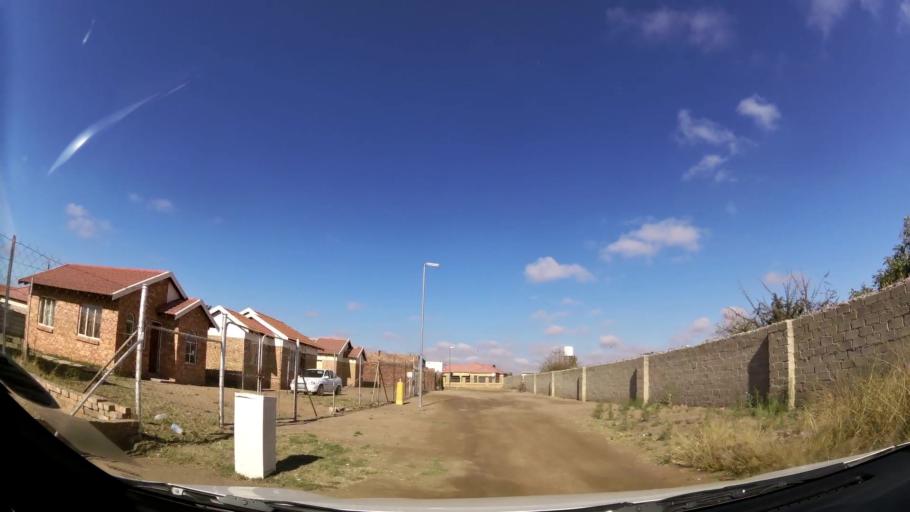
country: ZA
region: Limpopo
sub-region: Capricorn District Municipality
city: Polokwane
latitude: -23.8515
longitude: 29.4016
